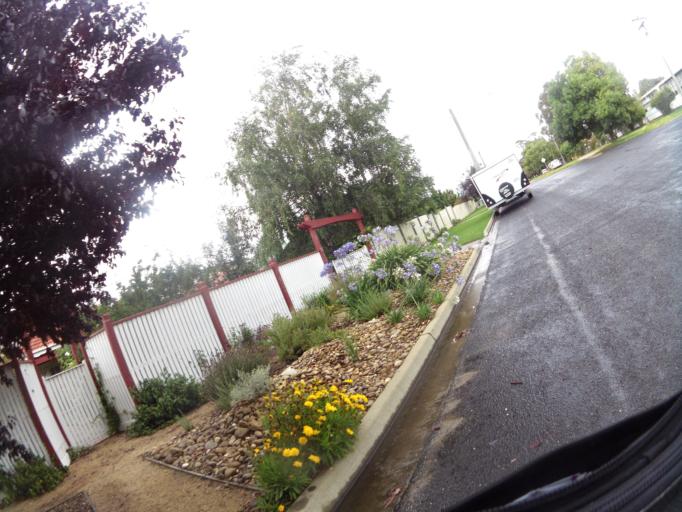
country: AU
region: Victoria
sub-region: East Gippsland
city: Bairnsdale
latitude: -37.8300
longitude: 147.6308
